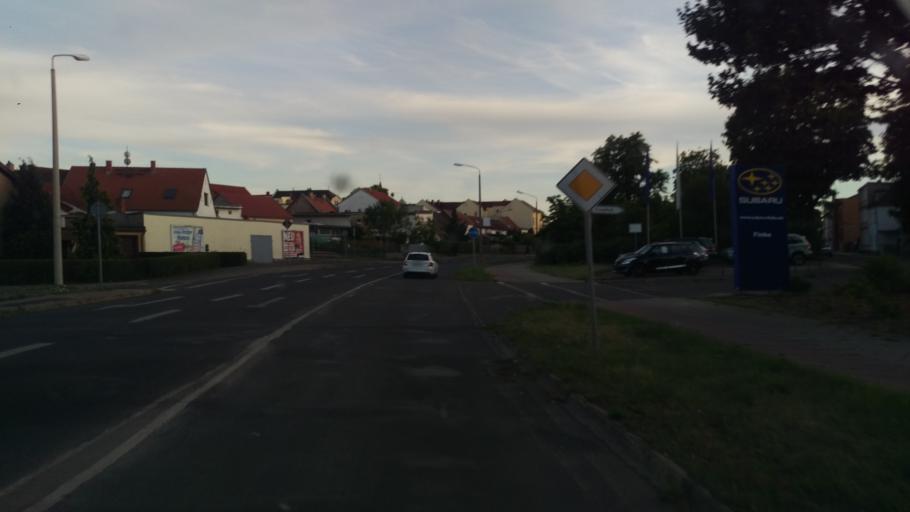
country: DE
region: Brandenburg
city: Eisenhuettenstadt
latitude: 52.1475
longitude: 14.6740
